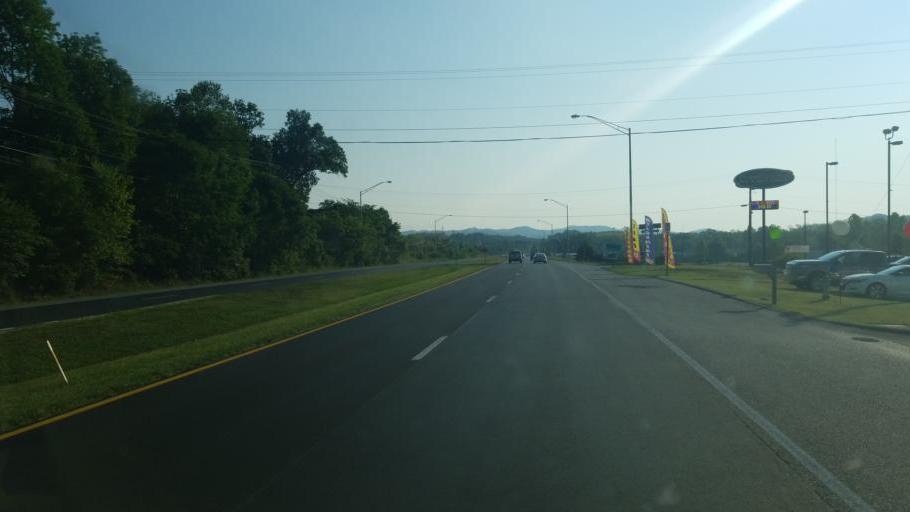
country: US
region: Tennessee
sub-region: Sullivan County
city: Bloomingdale
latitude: 36.5524
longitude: -82.4883
